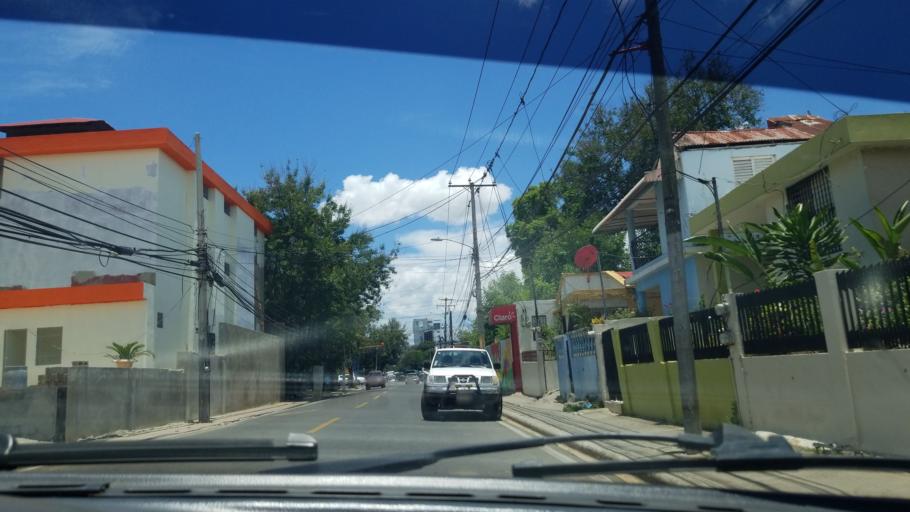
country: DO
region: Santiago
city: Santiago de los Caballeros
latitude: 19.4708
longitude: -70.6878
